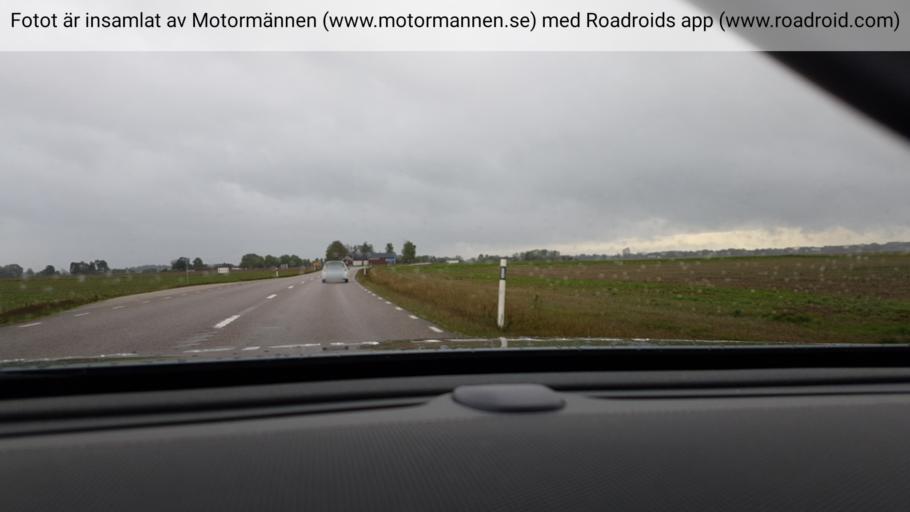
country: SE
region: Vaestra Goetaland
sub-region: Vanersborgs Kommun
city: Bralanda
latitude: 58.5807
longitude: 12.3967
